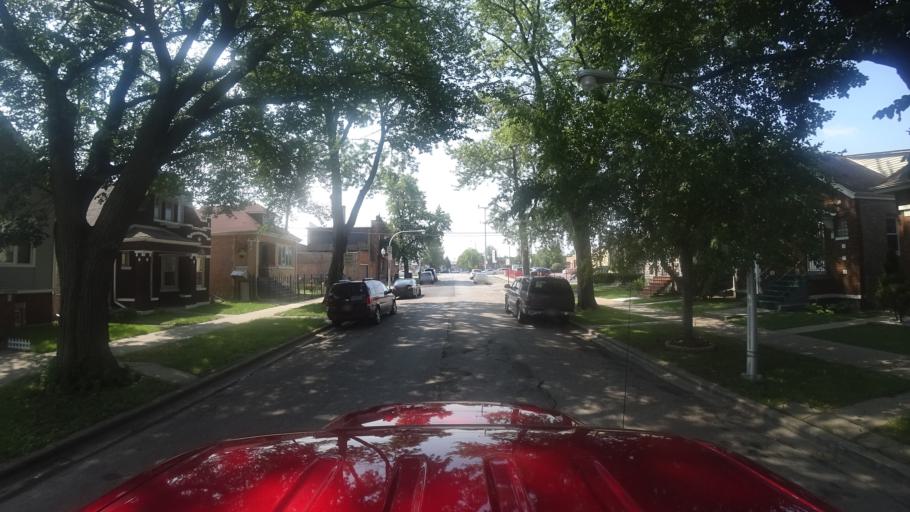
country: US
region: Illinois
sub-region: Cook County
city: Cicero
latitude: 41.8022
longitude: -87.7259
